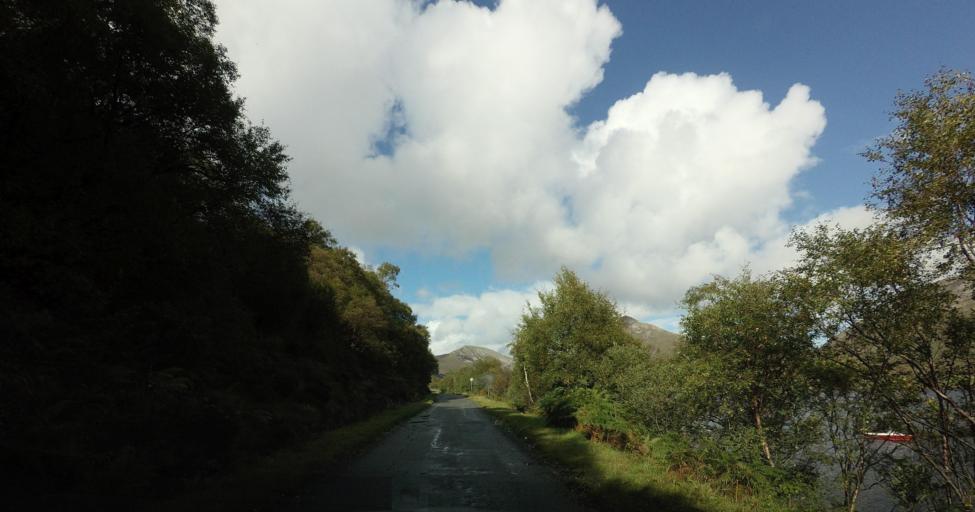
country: GB
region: Scotland
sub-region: Highland
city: Portree
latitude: 57.2132
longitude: -6.0364
